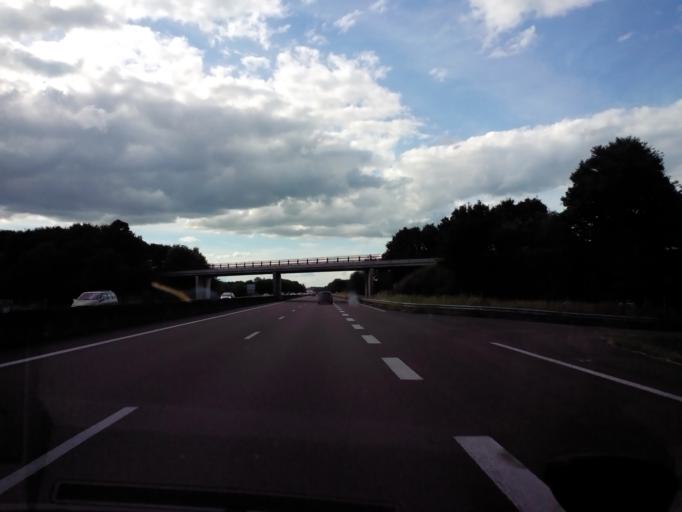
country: FR
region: Bourgogne
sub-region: Departement de la Cote-d'Or
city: Semur-en-Auxois
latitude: 47.3930
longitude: 4.3615
